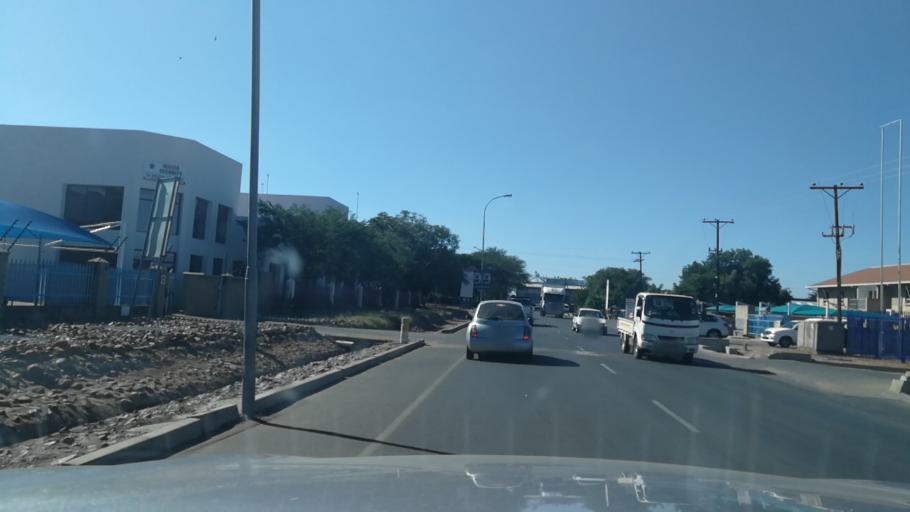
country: BW
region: South East
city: Gaborone
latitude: -24.6922
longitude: 25.8856
